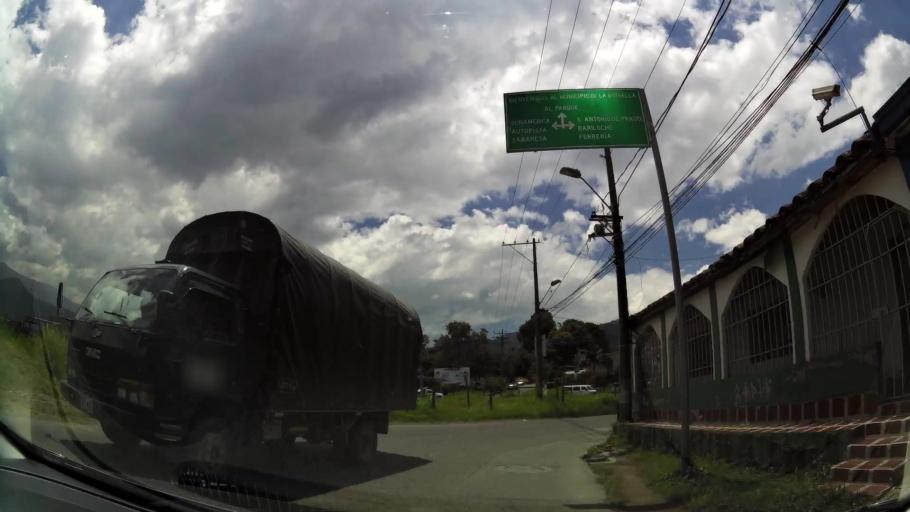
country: CO
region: Antioquia
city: La Estrella
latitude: 6.1618
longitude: -75.6361
